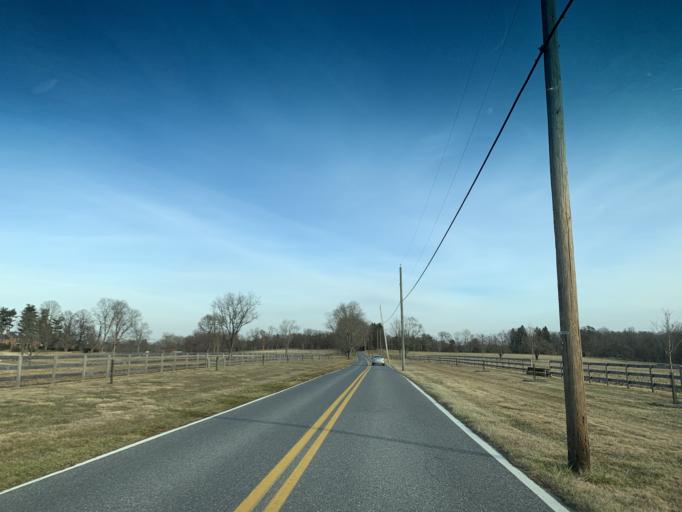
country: US
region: Maryland
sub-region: Harford County
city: Jarrettsville
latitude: 39.5574
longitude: -76.5594
